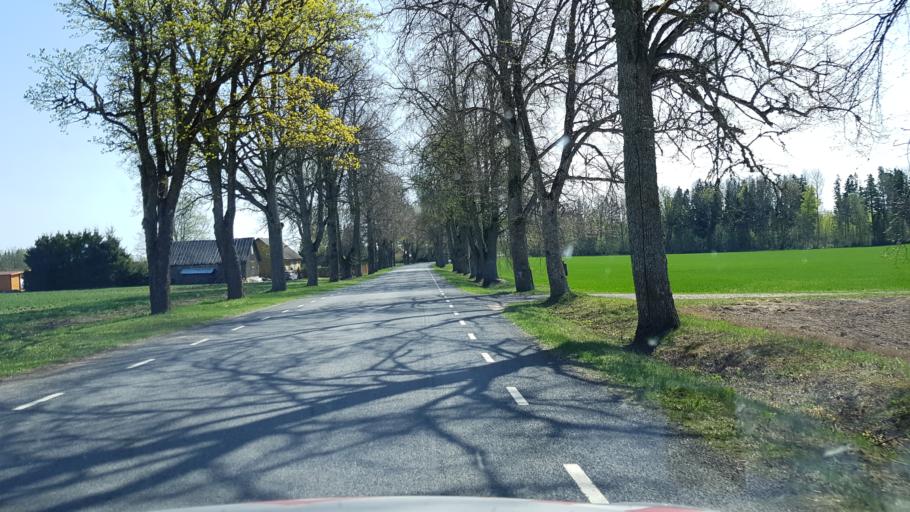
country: EE
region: Viljandimaa
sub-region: Vohma linn
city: Vohma
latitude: 58.5398
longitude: 25.5783
